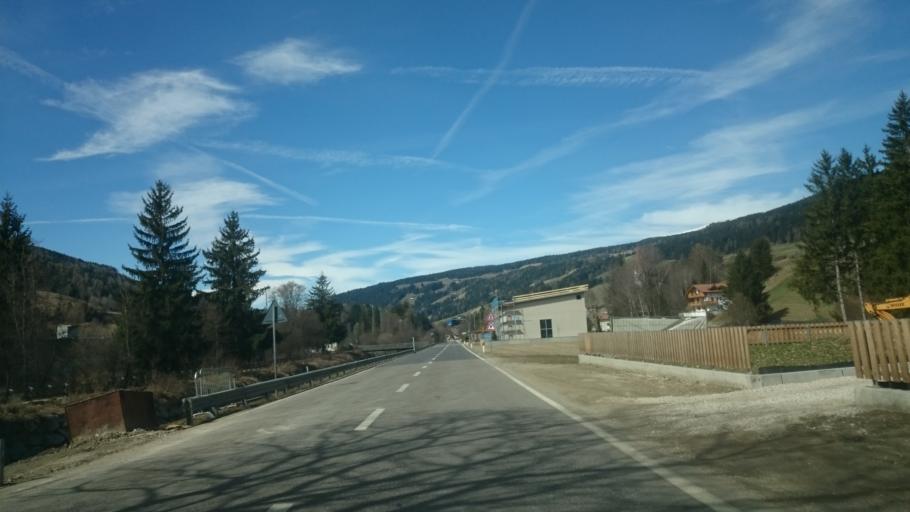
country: IT
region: Trentino-Alto Adige
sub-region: Bolzano
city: Monguelfo
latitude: 46.7519
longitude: 12.1141
